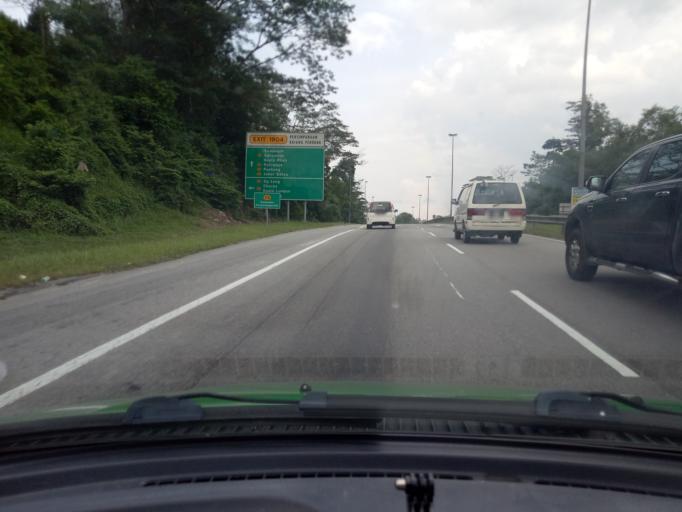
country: MY
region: Selangor
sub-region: Hulu Langat
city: Semenyih
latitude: 2.9890
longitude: 101.8224
